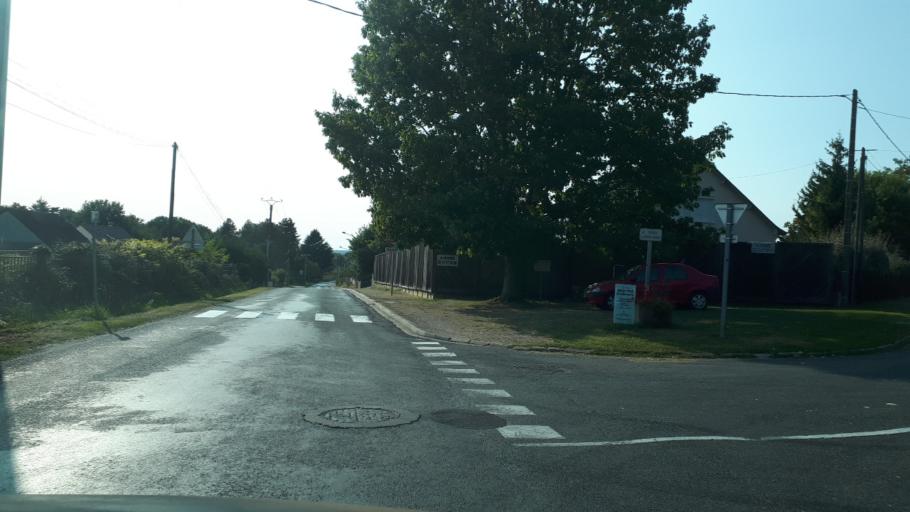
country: FR
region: Centre
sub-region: Departement du Cher
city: Saint-Eloy-de-Gy
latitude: 47.2239
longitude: 2.3272
